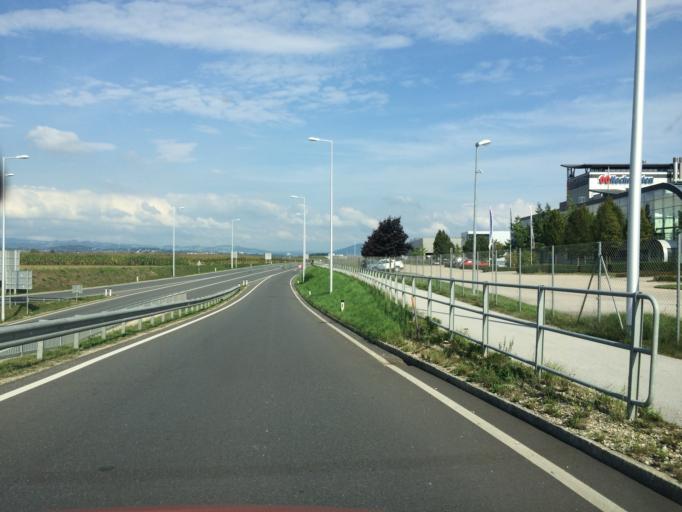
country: AT
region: Upper Austria
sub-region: Politischer Bezirk Linz-Land
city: Traun
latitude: 48.2443
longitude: 14.2233
